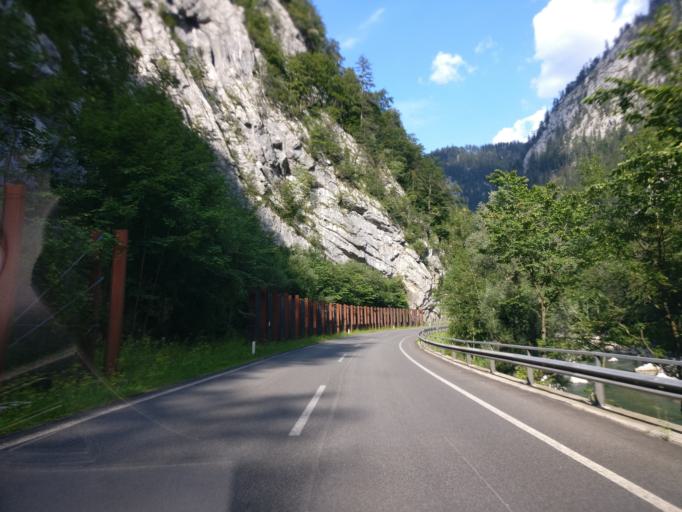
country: AT
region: Styria
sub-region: Politischer Bezirk Leoben
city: Hieflau
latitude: 47.5947
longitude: 14.7118
